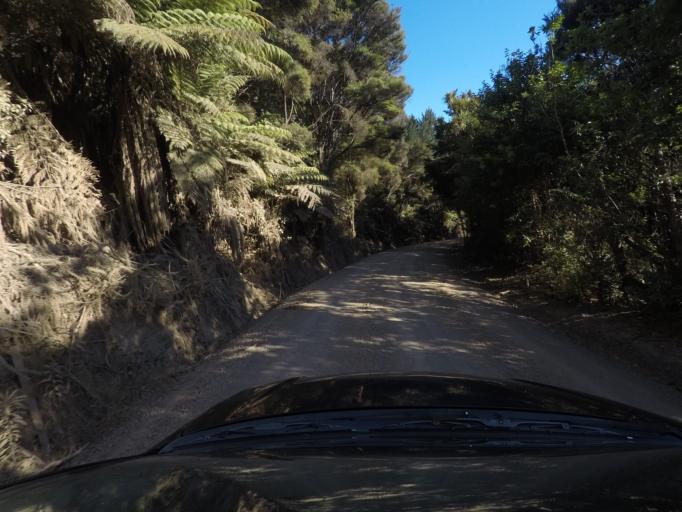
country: NZ
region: Northland
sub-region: Far North District
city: Paihia
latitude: -35.2557
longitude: 174.0707
